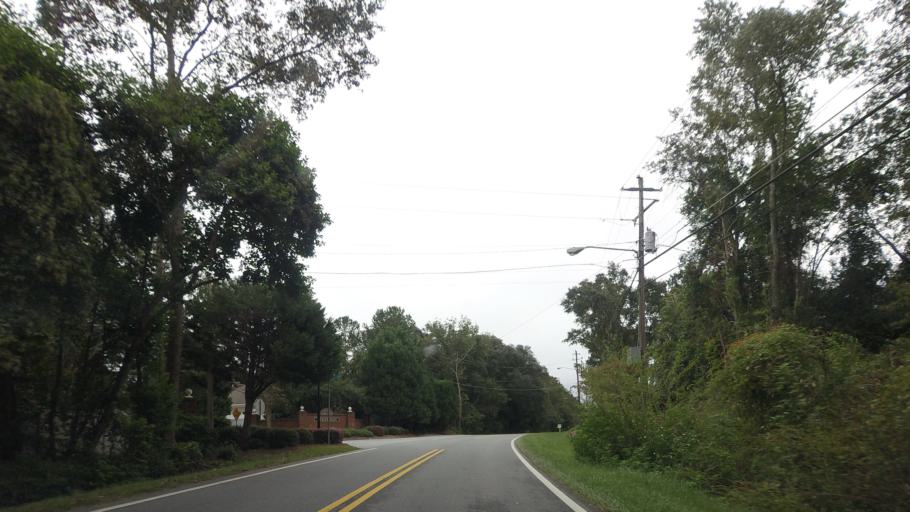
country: US
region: Georgia
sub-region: Lowndes County
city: Remerton
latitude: 30.8832
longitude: -83.3002
